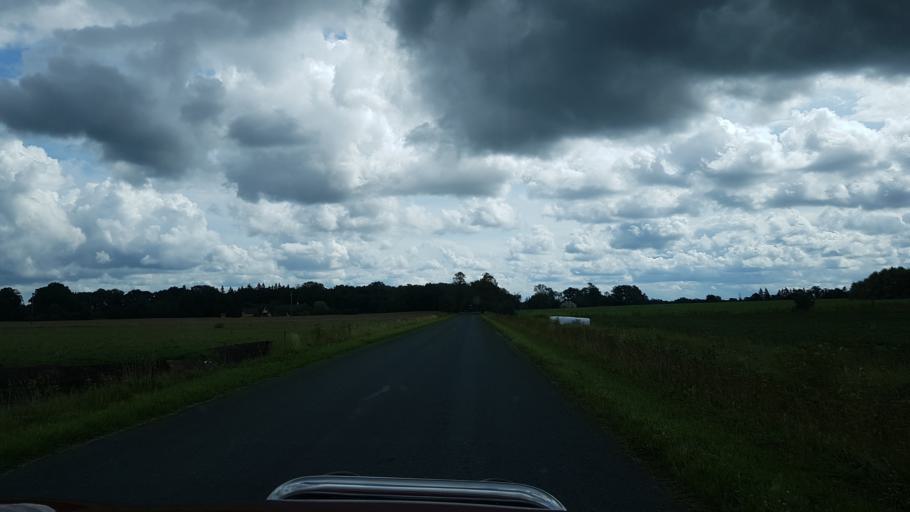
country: EE
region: Laeaene
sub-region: Lihula vald
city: Lihula
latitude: 58.7094
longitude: 24.0161
